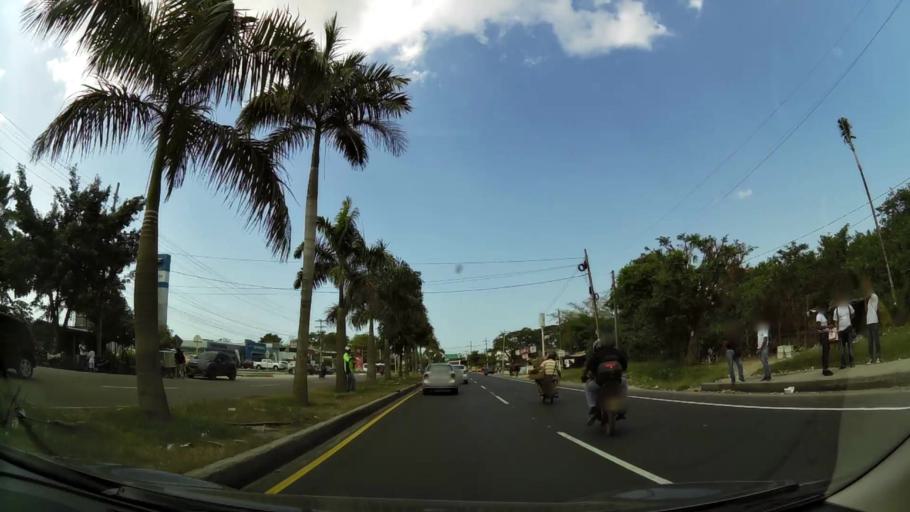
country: CO
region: Bolivar
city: Cartagena
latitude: 10.3753
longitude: -75.4592
